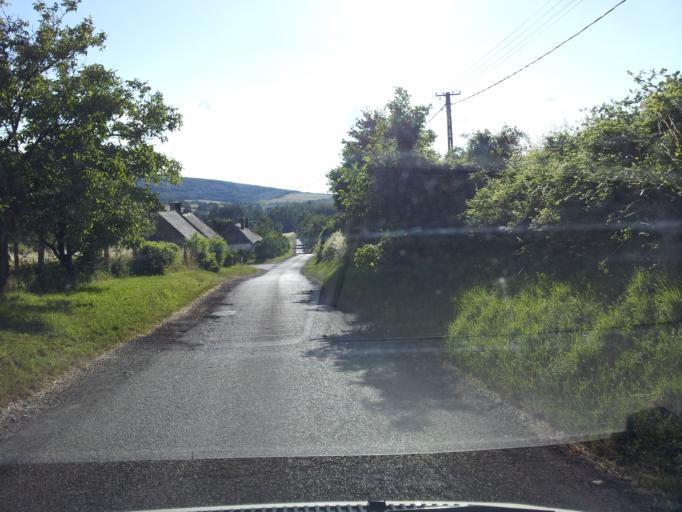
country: HU
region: Veszprem
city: Zirc
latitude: 47.2069
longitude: 17.8581
